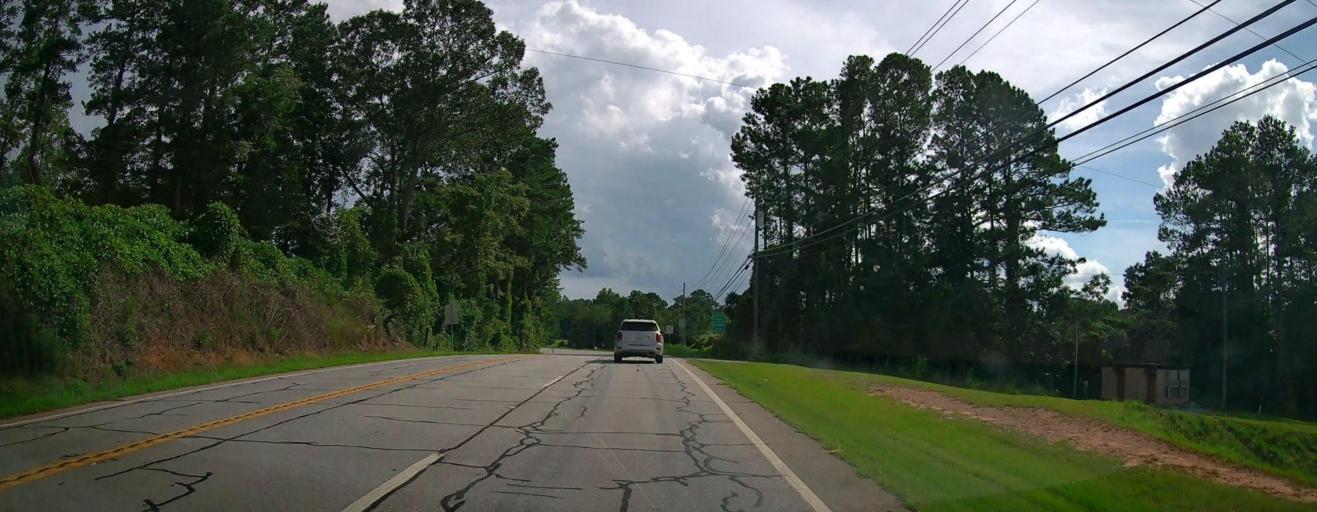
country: US
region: Georgia
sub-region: Harris County
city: Hamilton
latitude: 32.6086
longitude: -84.9124
